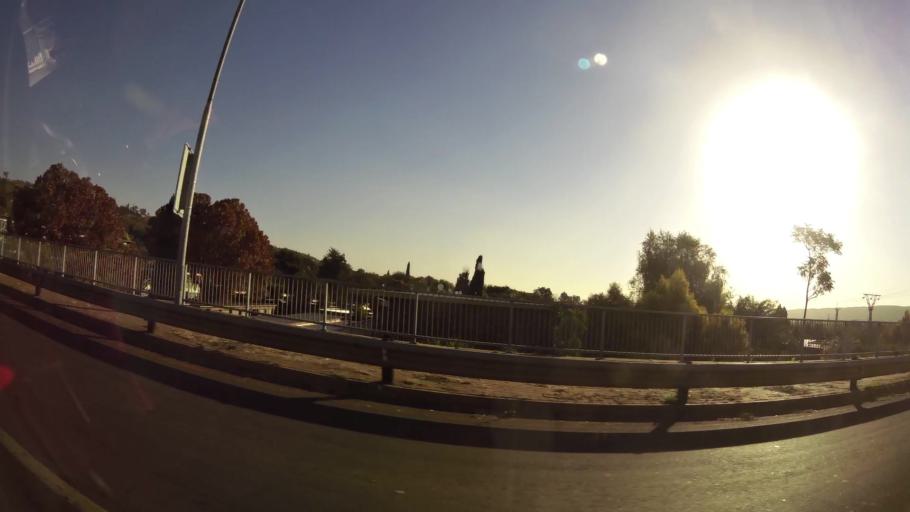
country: ZA
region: Gauteng
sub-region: City of Tshwane Metropolitan Municipality
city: Pretoria
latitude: -25.7202
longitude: 28.2423
